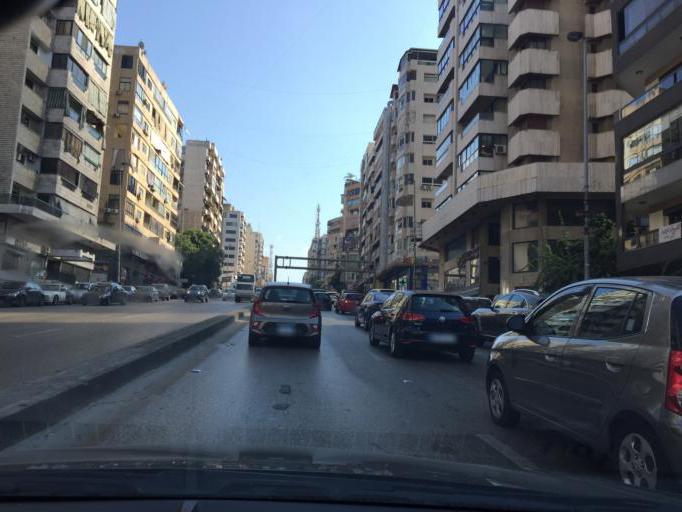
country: LB
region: Beyrouth
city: Beirut
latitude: 33.8906
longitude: 35.5004
